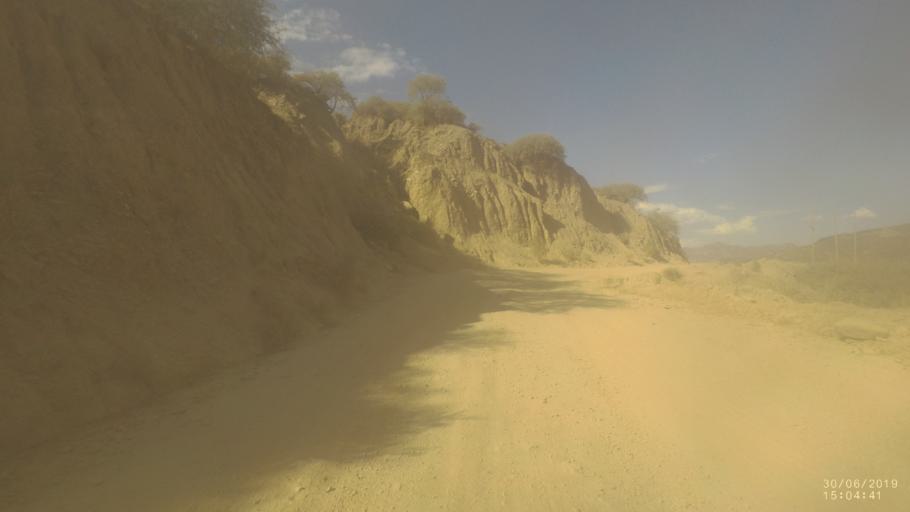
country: BO
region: Cochabamba
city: Irpa Irpa
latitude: -17.7321
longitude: -66.3202
